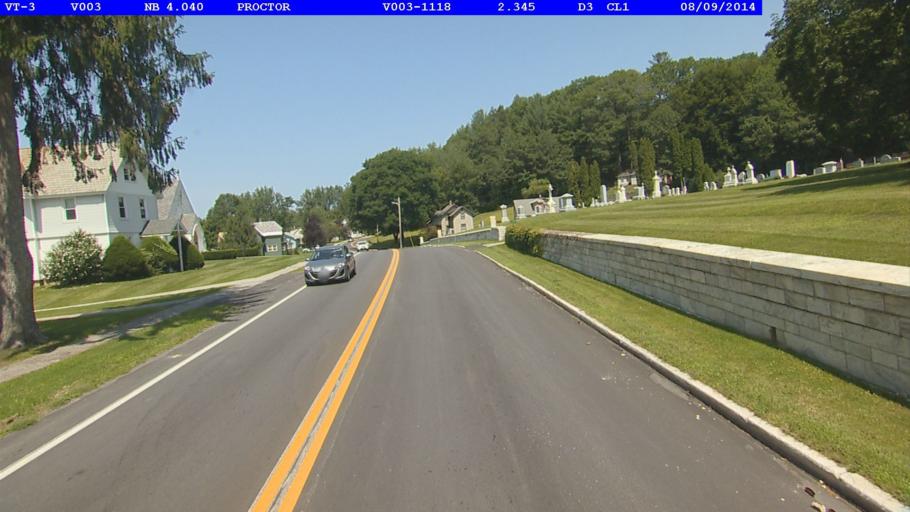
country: US
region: Vermont
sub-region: Rutland County
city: West Rutland
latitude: 43.6575
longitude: -73.0315
